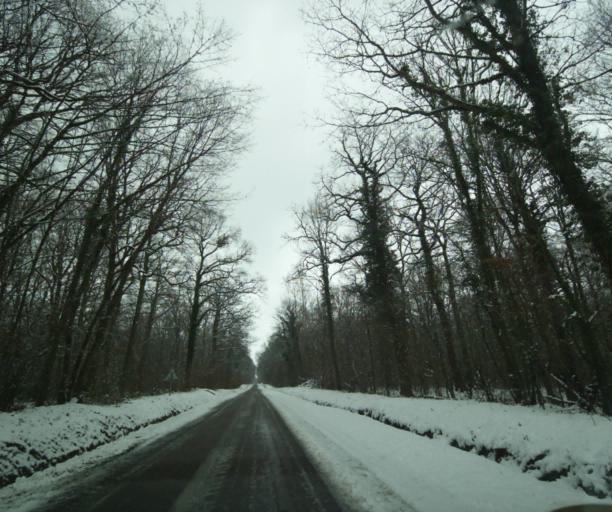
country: FR
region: Champagne-Ardenne
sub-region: Departement de la Haute-Marne
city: Laneuville-a-Remy
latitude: 48.3944
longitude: 4.8671
